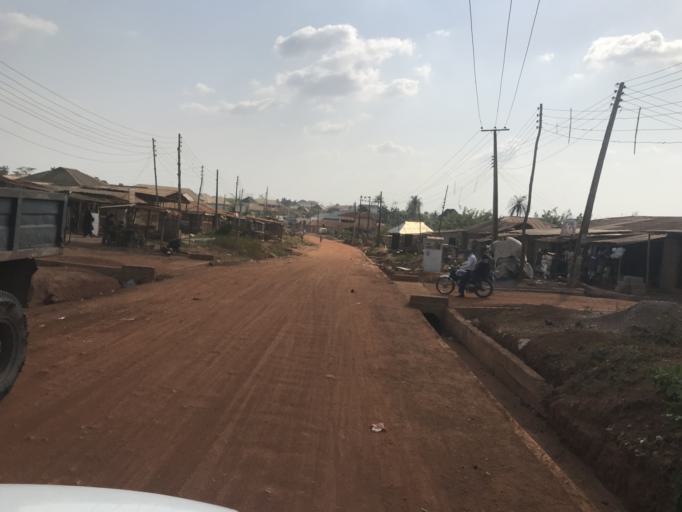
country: NG
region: Osun
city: Osogbo
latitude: 7.8144
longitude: 4.5605
